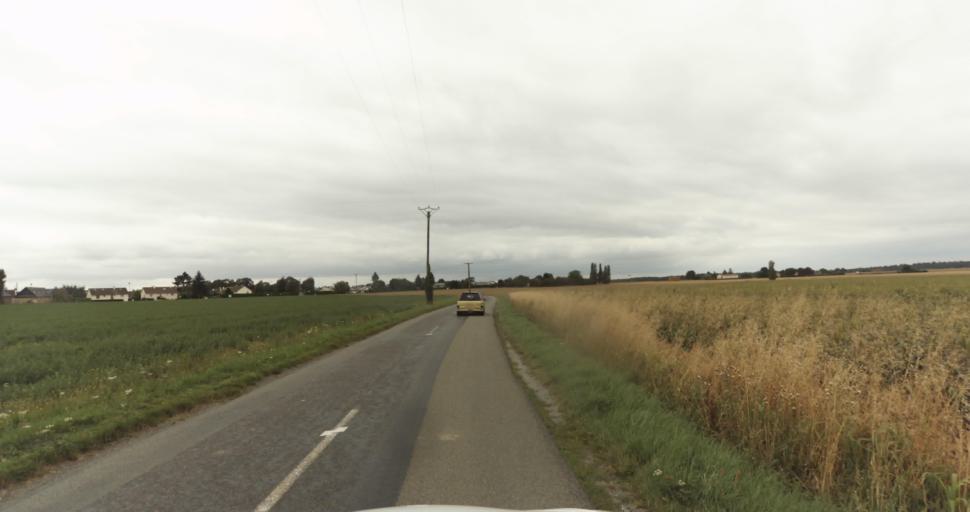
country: FR
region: Haute-Normandie
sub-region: Departement de l'Eure
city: Arnieres-sur-Iton
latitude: 48.9522
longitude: 1.1277
